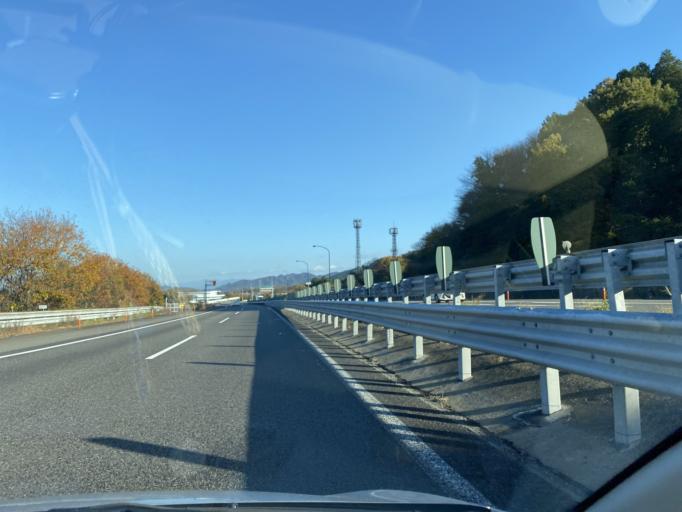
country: JP
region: Shiga Prefecture
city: Hikone
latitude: 35.1878
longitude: 136.2815
